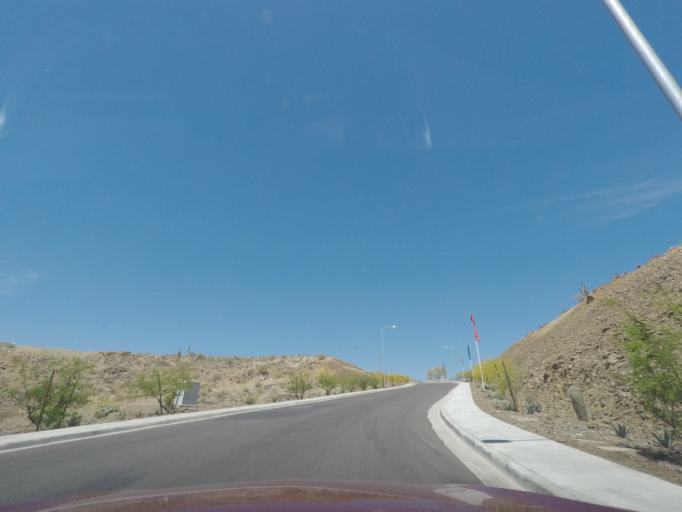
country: US
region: Arizona
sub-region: Maricopa County
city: Laveen
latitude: 33.2956
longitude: -112.1346
